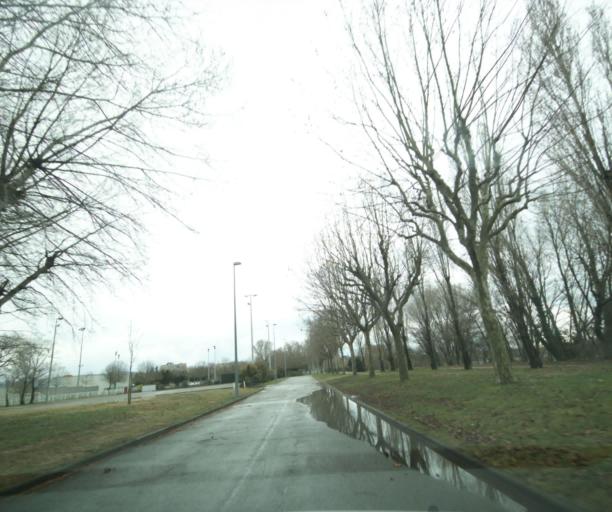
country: FR
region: Rhone-Alpes
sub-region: Departement de l'Ardeche
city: Guilherand-Granges
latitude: 44.9420
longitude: 4.8866
